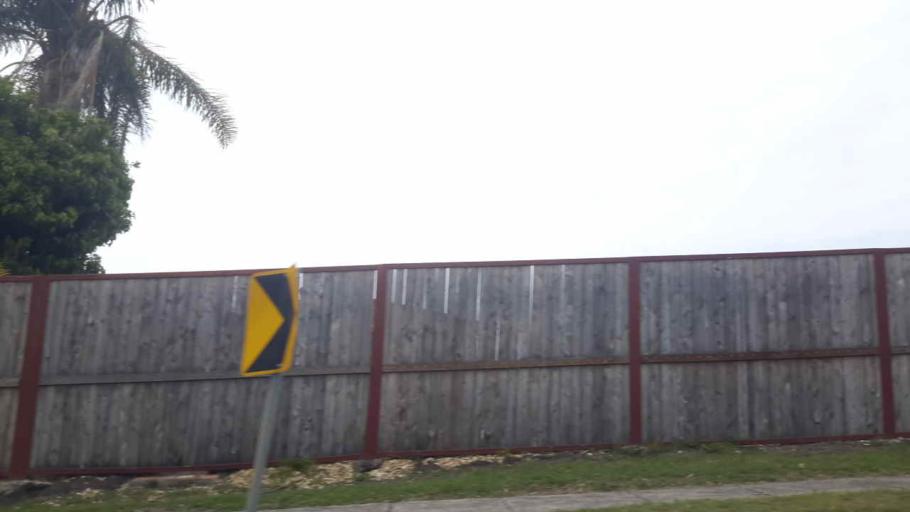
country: AU
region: New South Wales
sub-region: Wollongong
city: Bulli
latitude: -34.3527
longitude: 150.9025
